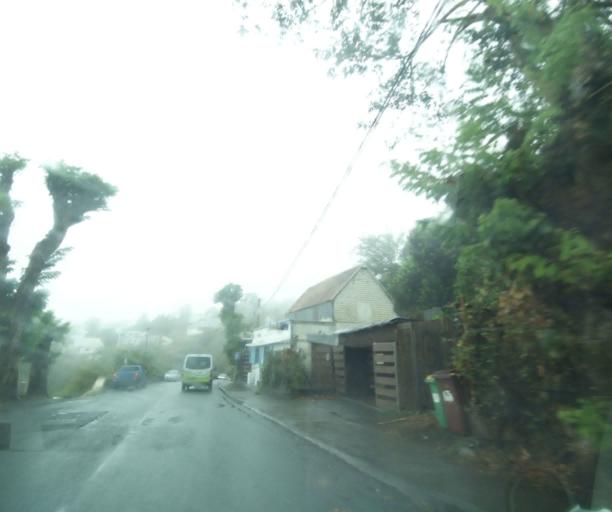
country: RE
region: Reunion
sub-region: Reunion
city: Saint-Paul
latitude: -20.9971
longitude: 55.3273
